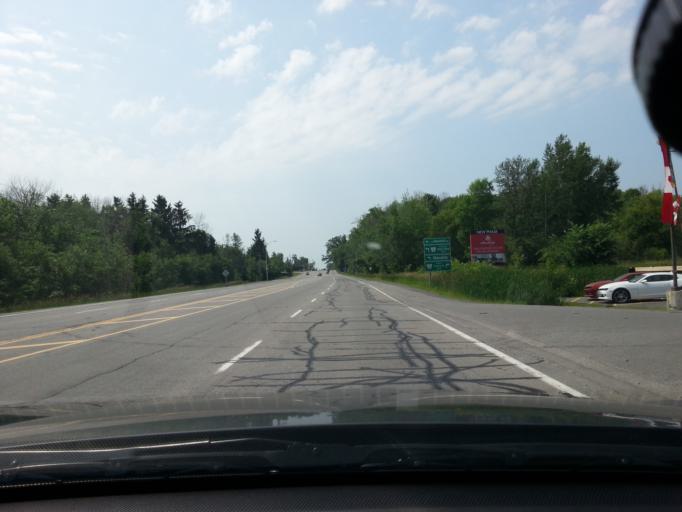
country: CA
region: Ontario
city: Bells Corners
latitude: 45.2516
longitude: -75.7105
